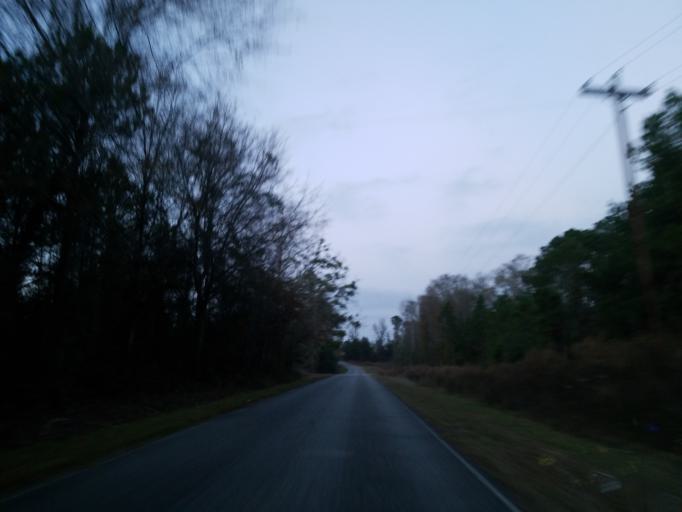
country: US
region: Alabama
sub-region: Sumter County
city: York
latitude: 32.4102
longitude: -88.4403
